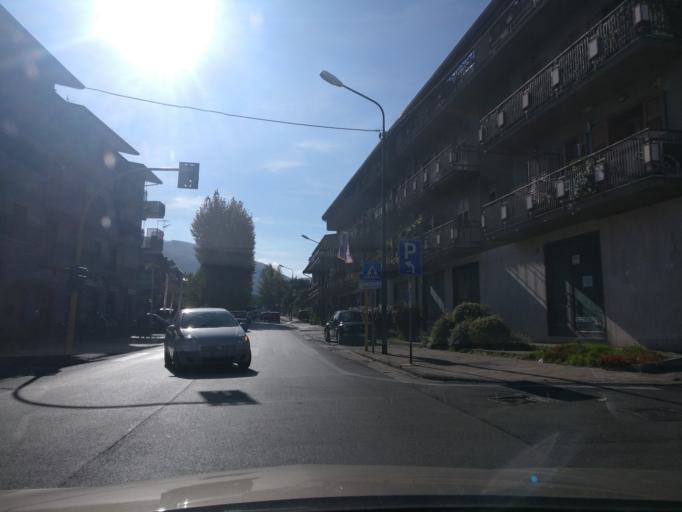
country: IT
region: Campania
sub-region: Provincia di Avellino
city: Monteforte Irpino
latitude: 40.9042
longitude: 14.7436
